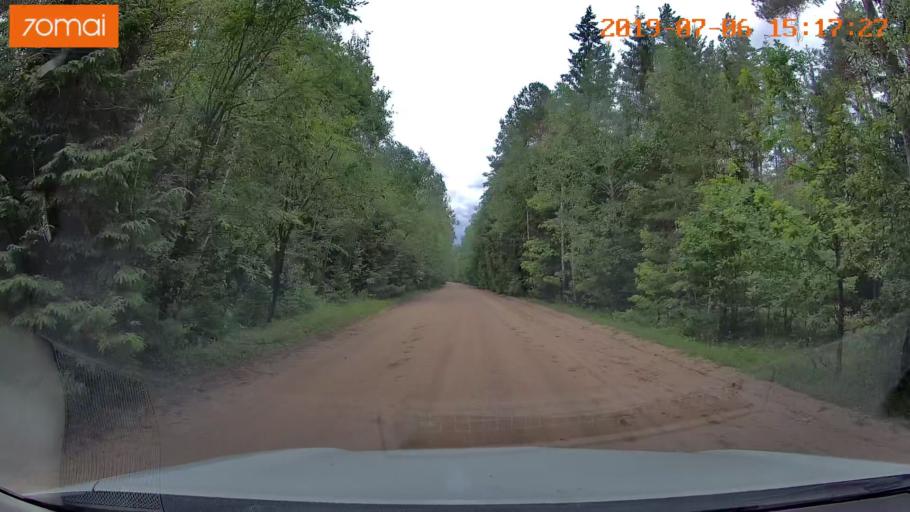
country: BY
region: Minsk
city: Ivyanyets
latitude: 53.9882
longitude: 26.6659
